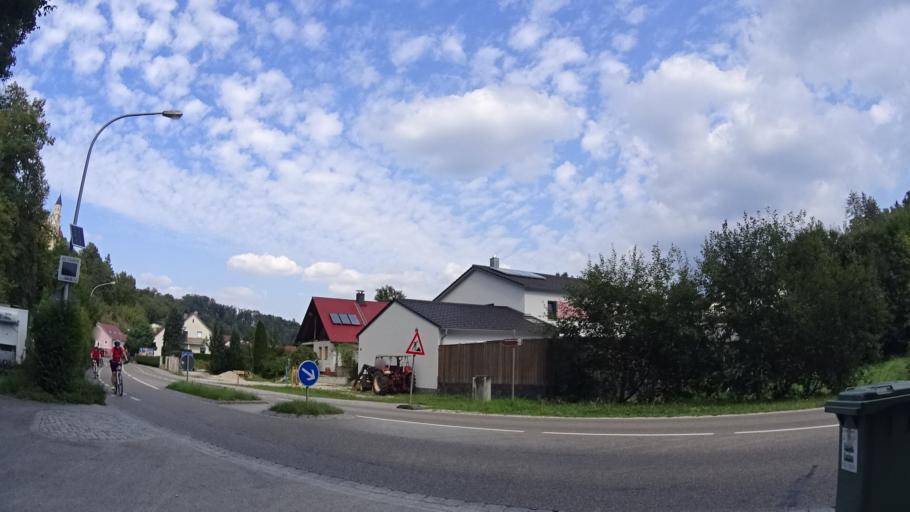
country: DE
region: Bavaria
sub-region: Lower Bavaria
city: Riedenburg
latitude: 48.9191
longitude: 11.6829
